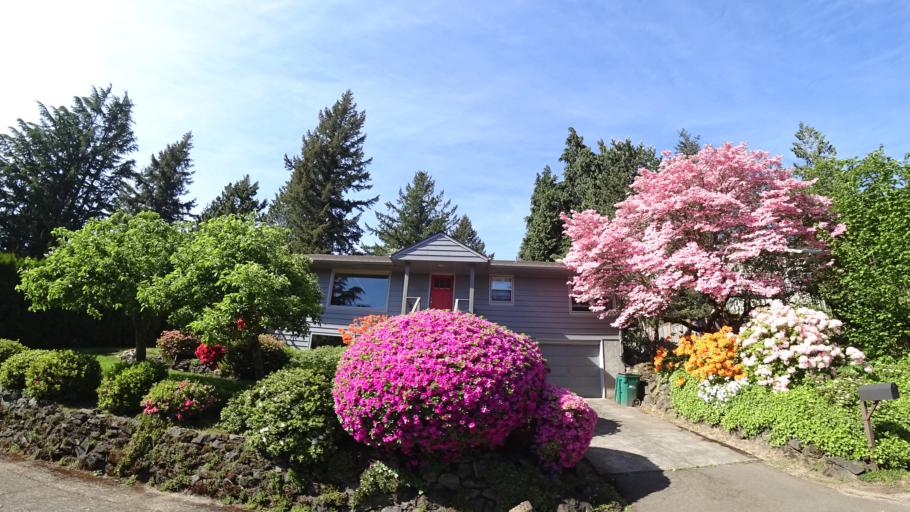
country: US
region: Oregon
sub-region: Washington County
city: West Slope
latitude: 45.4976
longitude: -122.7509
